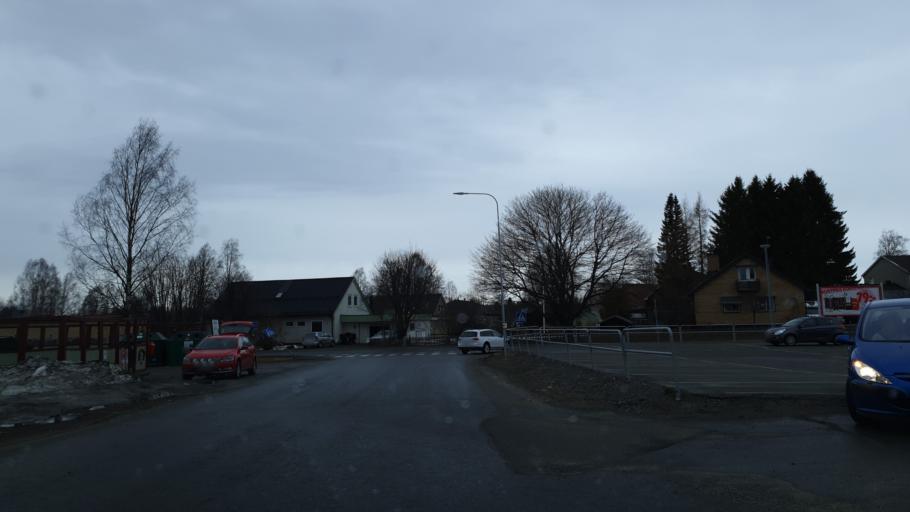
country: SE
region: Vaesterbotten
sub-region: Skelleftea Kommun
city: Kage
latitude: 64.8318
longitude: 20.9872
